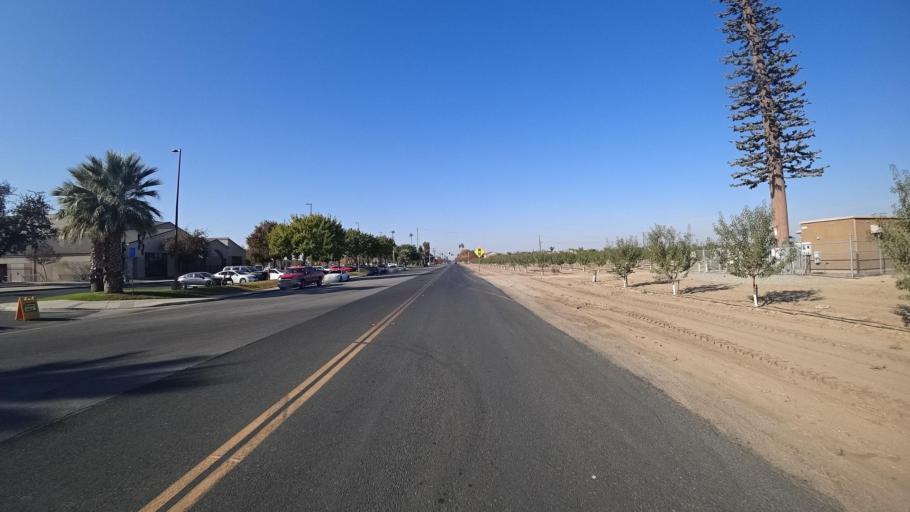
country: US
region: California
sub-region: Kern County
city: Delano
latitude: 35.7687
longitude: -119.2204
